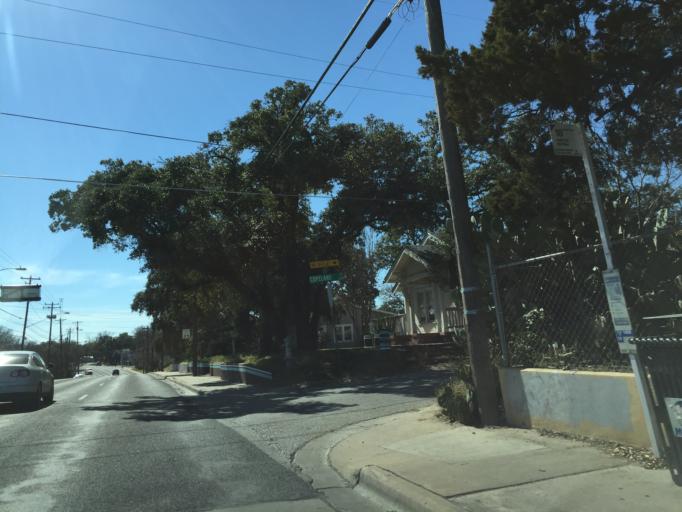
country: US
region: Texas
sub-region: Travis County
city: Austin
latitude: 30.2536
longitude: -97.7531
